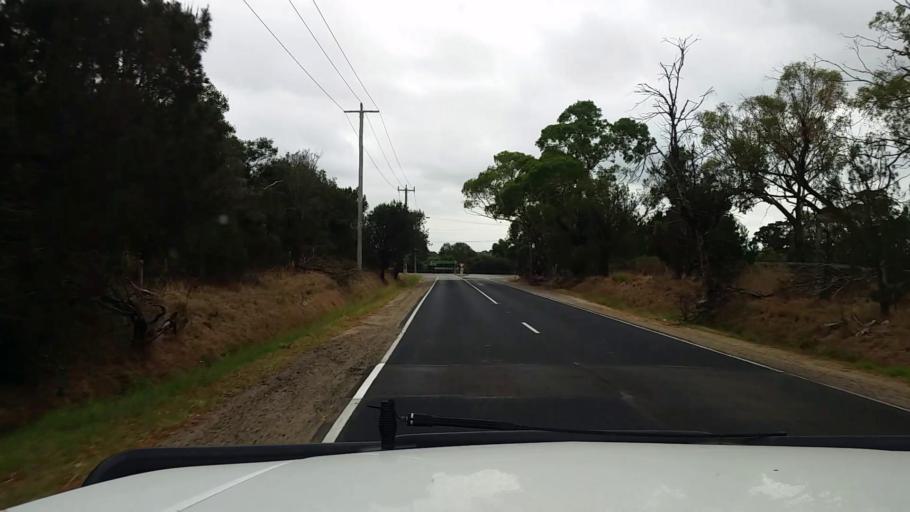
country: AU
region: Victoria
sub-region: Mornington Peninsula
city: Baxter
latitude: -38.2061
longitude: 145.1585
